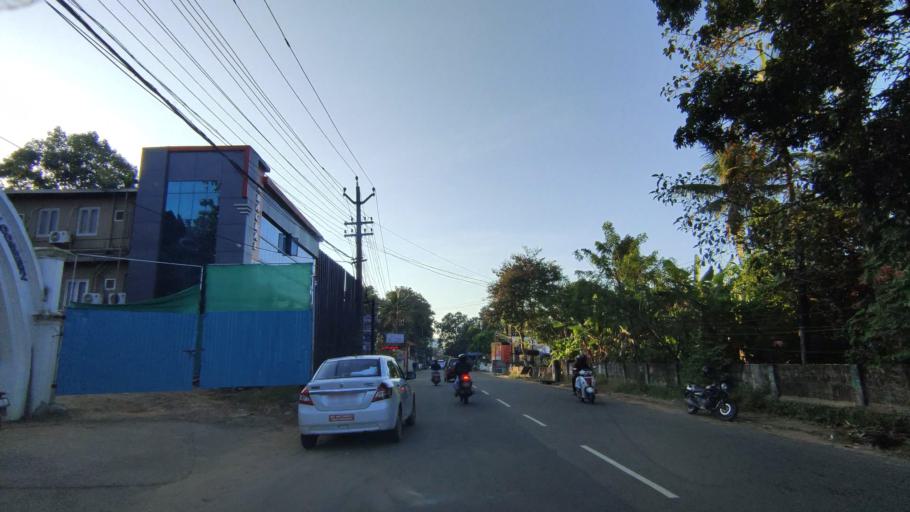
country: IN
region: Kerala
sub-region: Kottayam
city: Kottayam
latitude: 9.6030
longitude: 76.5169
